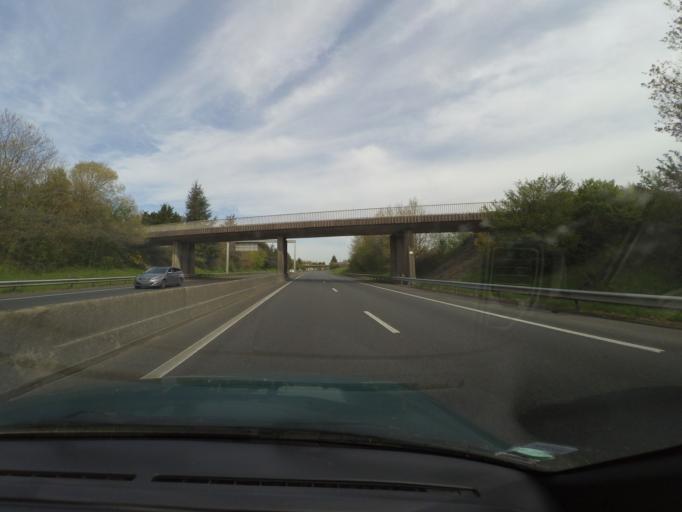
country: FR
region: Pays de la Loire
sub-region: Departement de la Loire-Atlantique
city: Les Sorinieres
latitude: 47.1358
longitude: -1.5103
